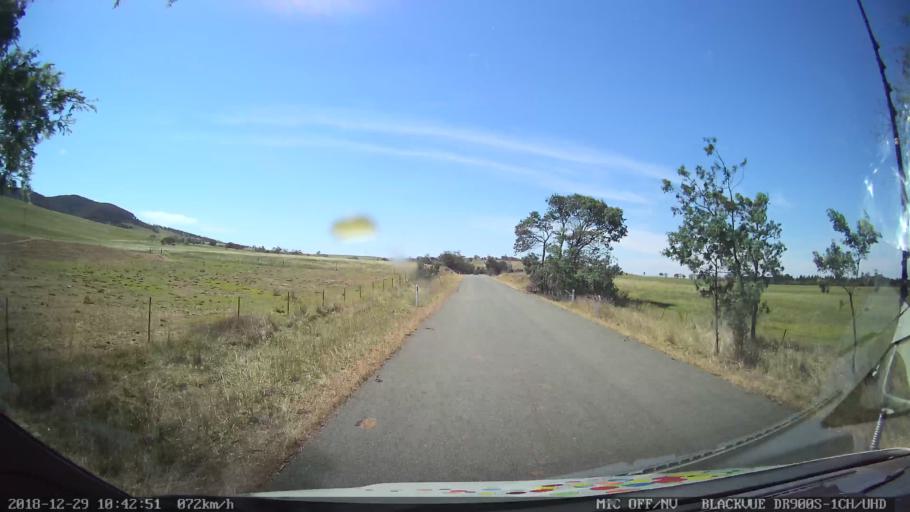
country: AU
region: New South Wales
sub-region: Palerang
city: Bungendore
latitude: -35.0366
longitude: 149.5343
